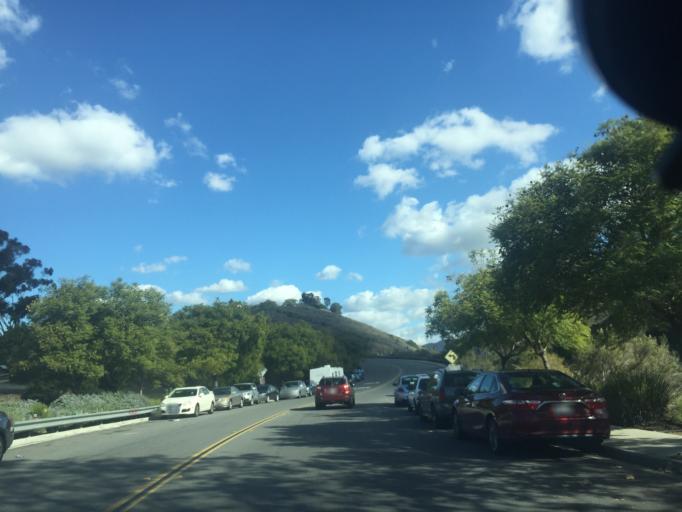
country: US
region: California
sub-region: San Diego County
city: La Mesa
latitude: 32.7831
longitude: -117.0863
